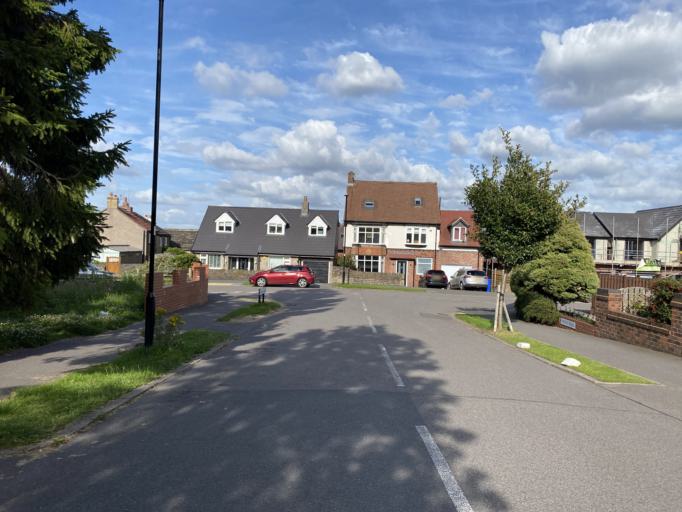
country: GB
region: England
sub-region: Sheffield
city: Sheffield
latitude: 53.3585
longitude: -1.5147
